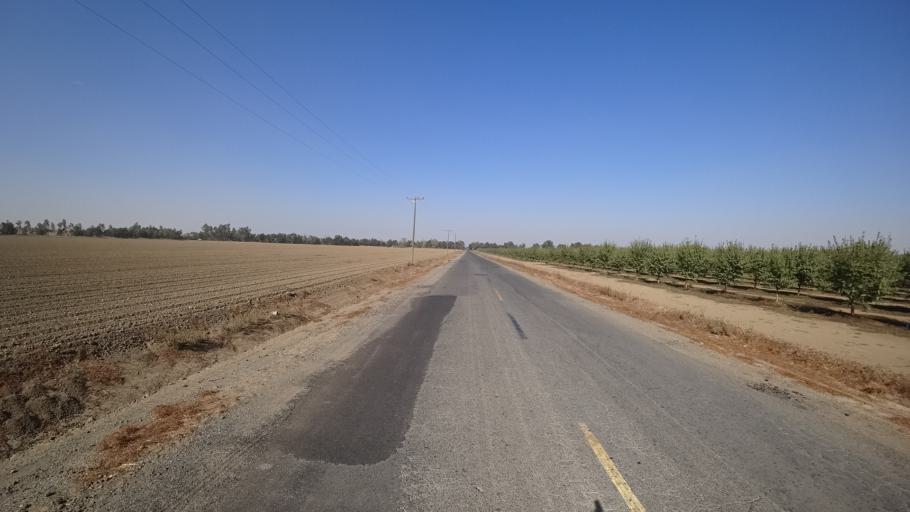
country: US
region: California
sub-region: Yolo County
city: Woodland
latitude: 38.7303
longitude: -121.8490
